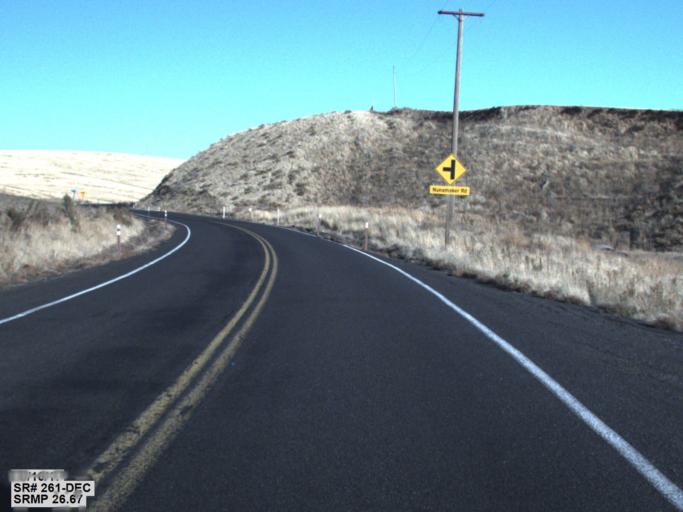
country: US
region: Washington
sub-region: Adams County
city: Ritzville
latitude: 46.6776
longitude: -118.3772
